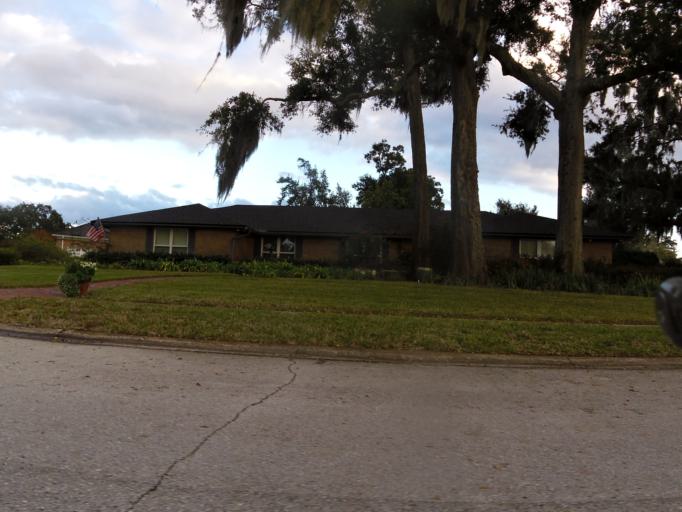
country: US
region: Florida
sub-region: Duval County
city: Jacksonville
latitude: 30.2787
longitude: -81.6633
